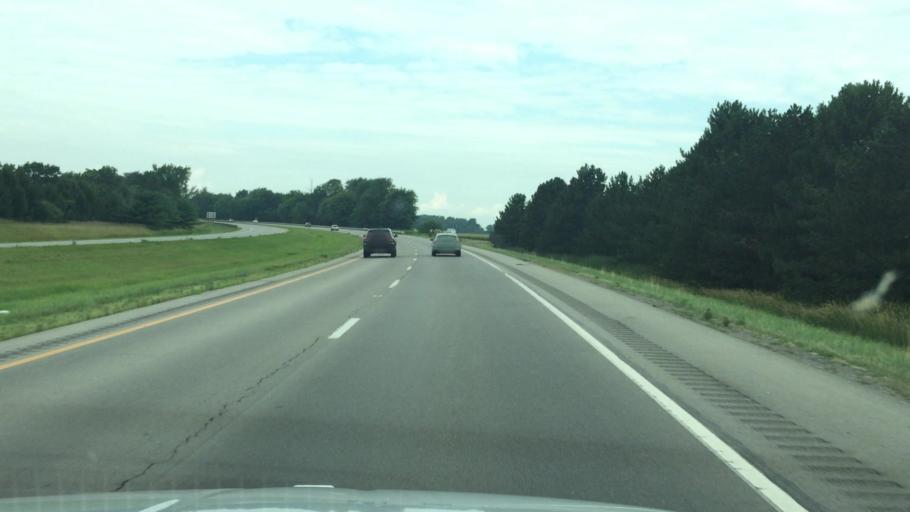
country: US
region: Ohio
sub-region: Wyandot County
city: Carey
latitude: 40.9798
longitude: -83.4956
